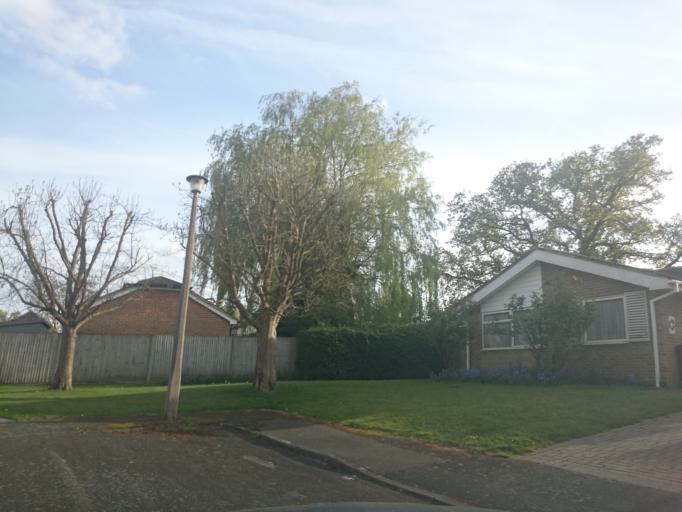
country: GB
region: England
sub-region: Surrey
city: Seale
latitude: 51.2382
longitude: -0.7070
